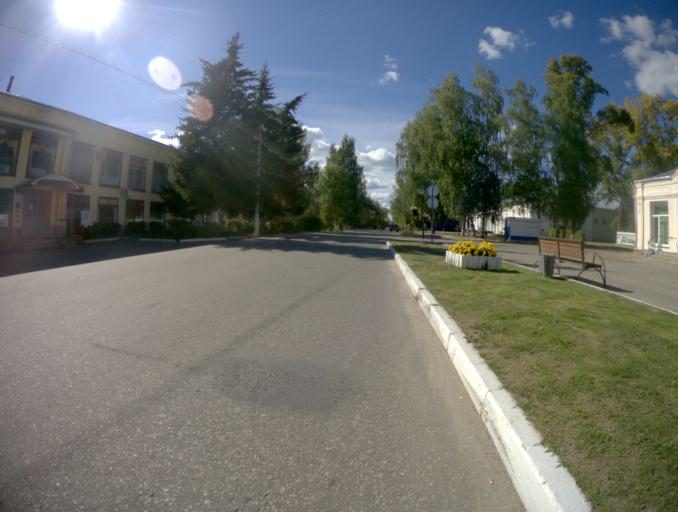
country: RU
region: Vladimir
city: Krasnaya Gorbatka
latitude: 55.8648
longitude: 41.7640
